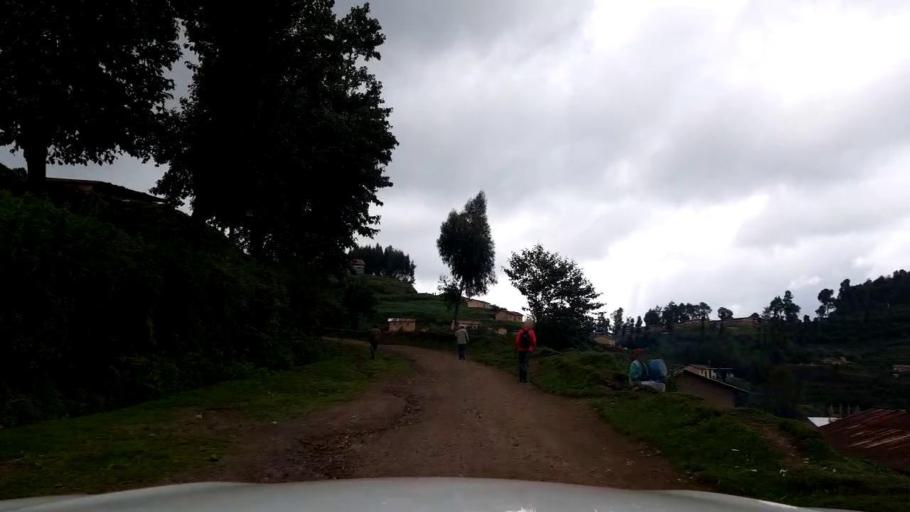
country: RW
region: Western Province
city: Gisenyi
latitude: -1.6739
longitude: 29.4117
